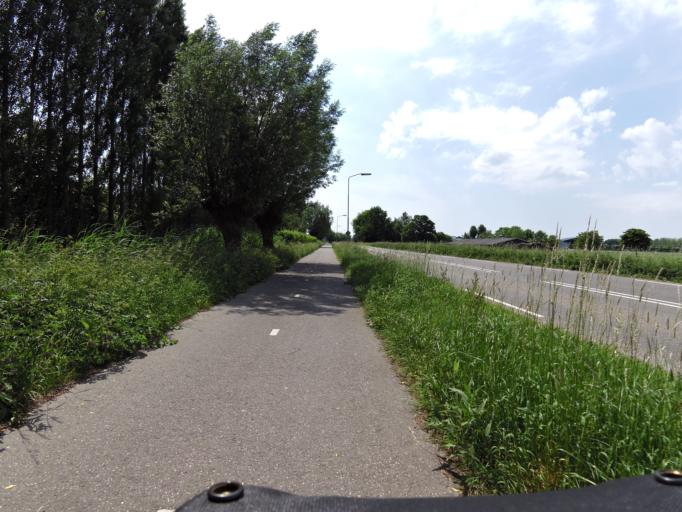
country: NL
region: North Brabant
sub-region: Gemeente Aalburg
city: Aalburg
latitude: 51.8125
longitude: 5.0903
